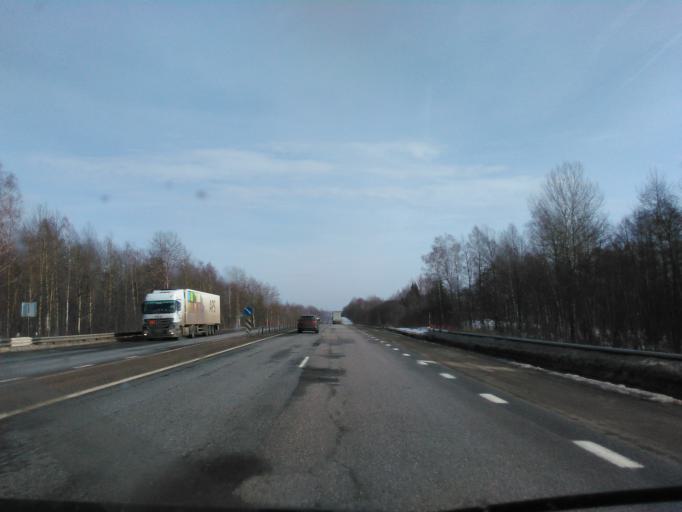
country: BY
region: Vitebsk
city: Dubrowna
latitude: 54.6862
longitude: 30.8344
